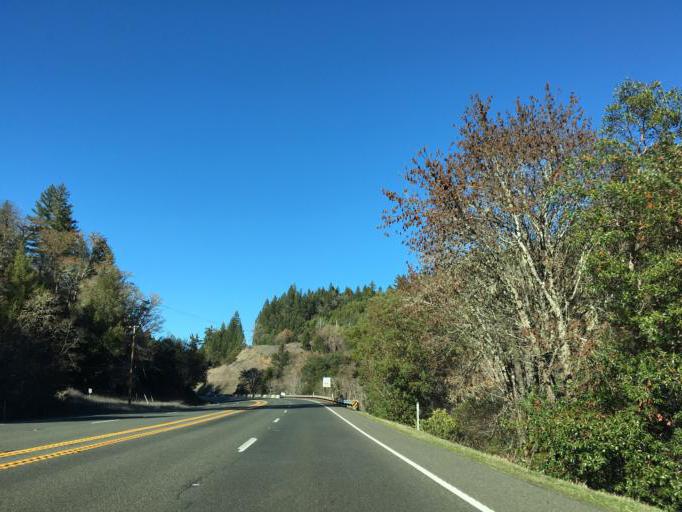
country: US
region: California
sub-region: Mendocino County
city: Brooktrails
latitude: 39.5615
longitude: -123.4330
